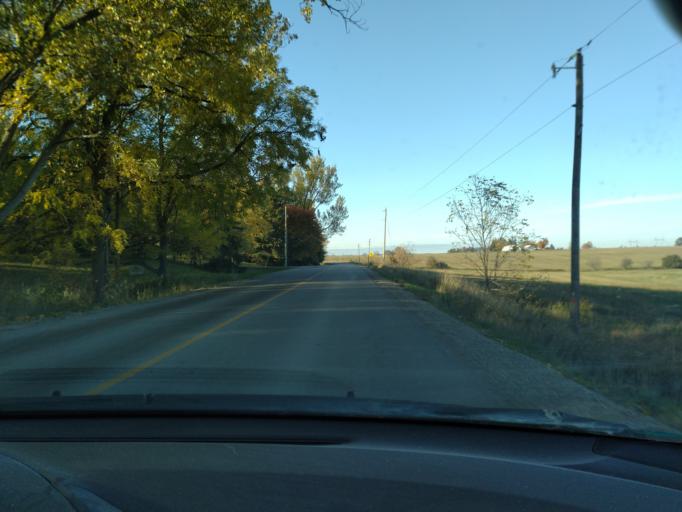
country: CA
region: Ontario
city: Bradford West Gwillimbury
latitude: 44.0669
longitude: -79.7383
